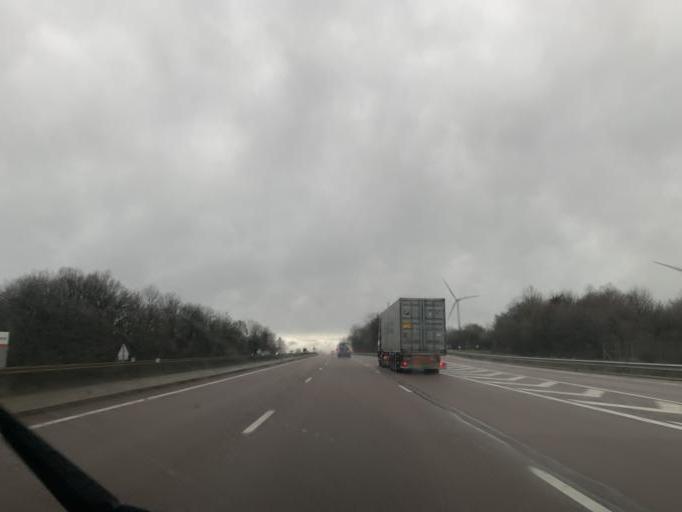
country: FR
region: Bourgogne
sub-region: Departement de la Cote-d'Or
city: Selongey
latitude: 47.6880
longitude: 5.1828
